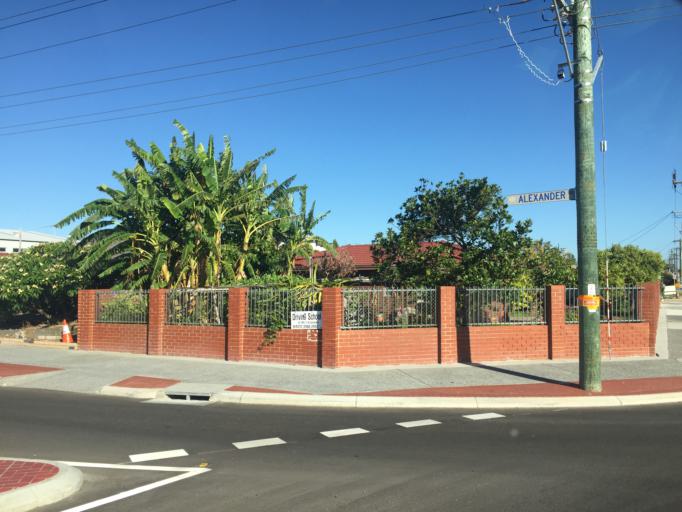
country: AU
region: Western Australia
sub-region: Belmont
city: Rivervale
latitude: -31.9612
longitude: 115.9282
